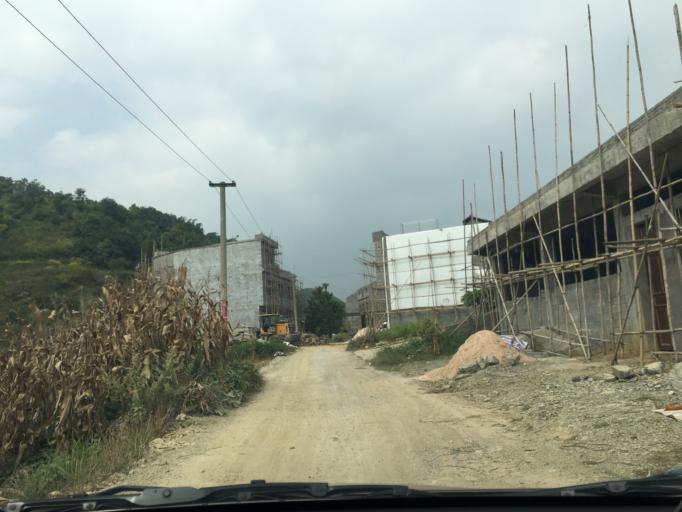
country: CN
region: Guizhou Sheng
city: Anshun
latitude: 25.5736
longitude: 105.6335
